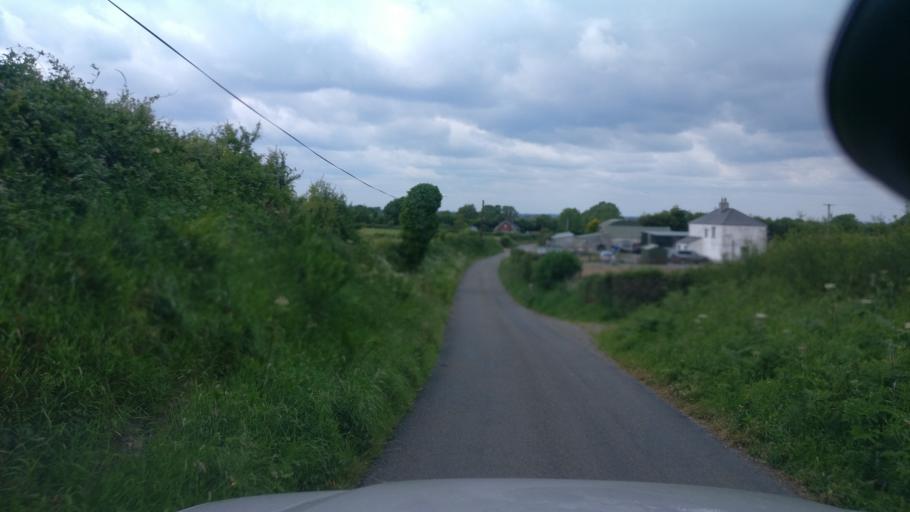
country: IE
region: Connaught
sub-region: County Galway
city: Ballinasloe
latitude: 53.2964
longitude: -8.3177
